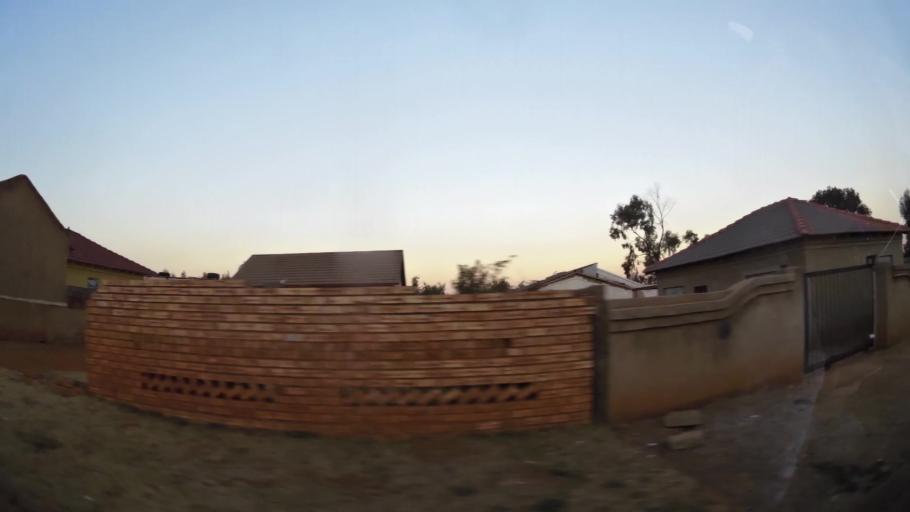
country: ZA
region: Gauteng
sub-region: West Rand District Municipality
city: Randfontein
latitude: -26.2117
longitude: 27.7185
